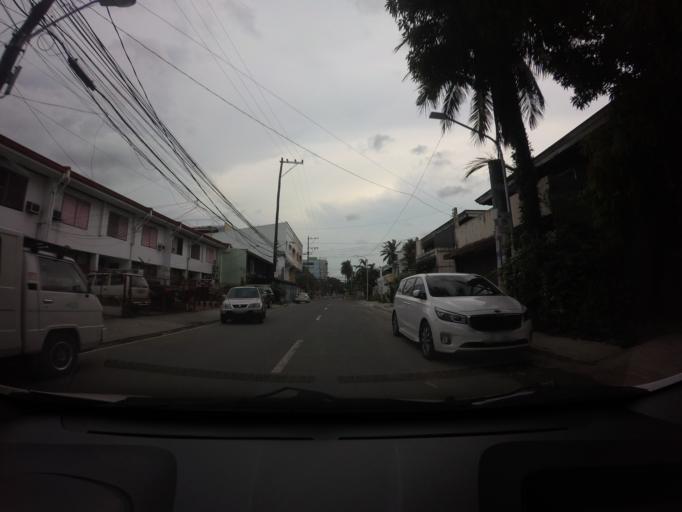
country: PH
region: Calabarzon
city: Del Monte
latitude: 14.6199
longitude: 121.0077
